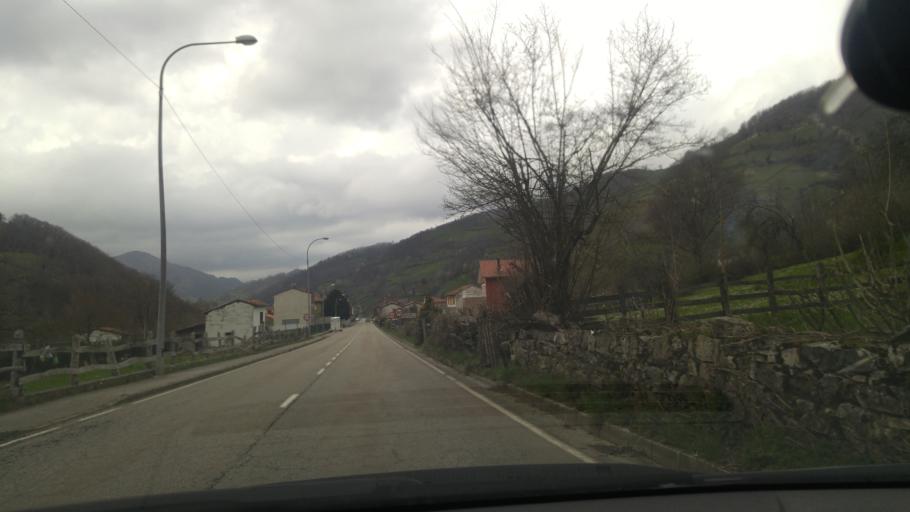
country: ES
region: Asturias
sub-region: Province of Asturias
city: Rio Aller
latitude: 43.1122
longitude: -5.5274
